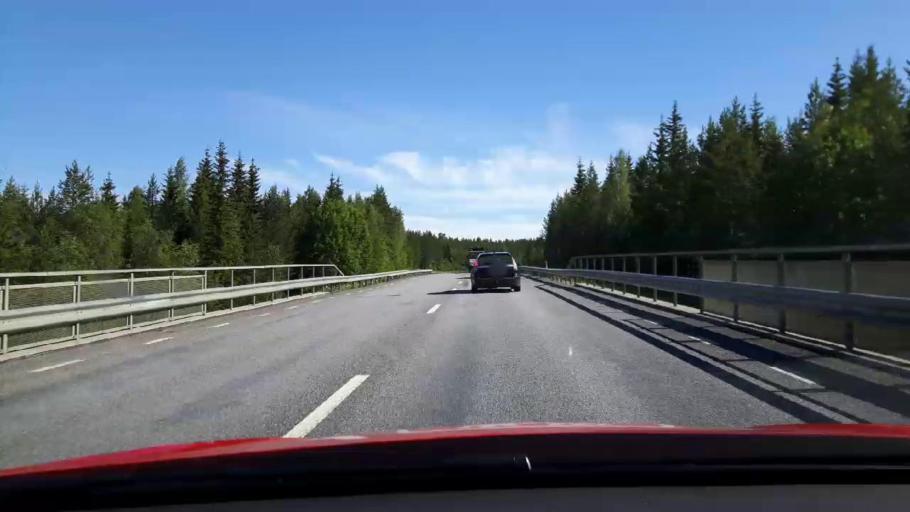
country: SE
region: Jaemtland
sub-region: OEstersunds Kommun
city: Lit
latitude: 63.3829
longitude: 14.8912
